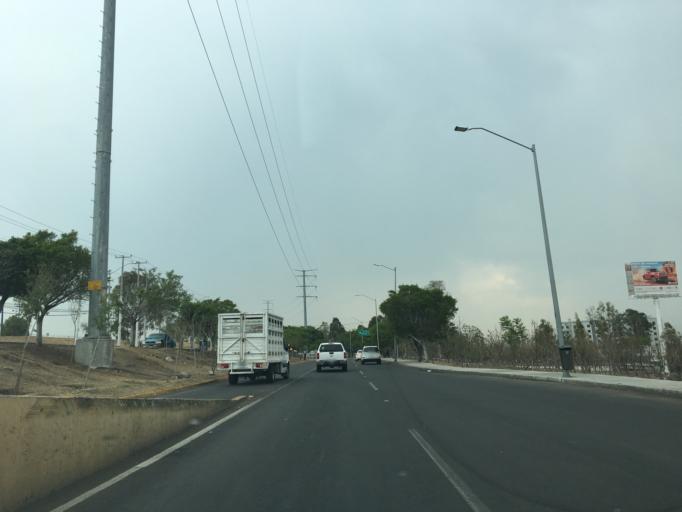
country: MX
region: Queretaro
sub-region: Queretaro
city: Santiago de Queretaro
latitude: 20.5803
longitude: -100.3653
